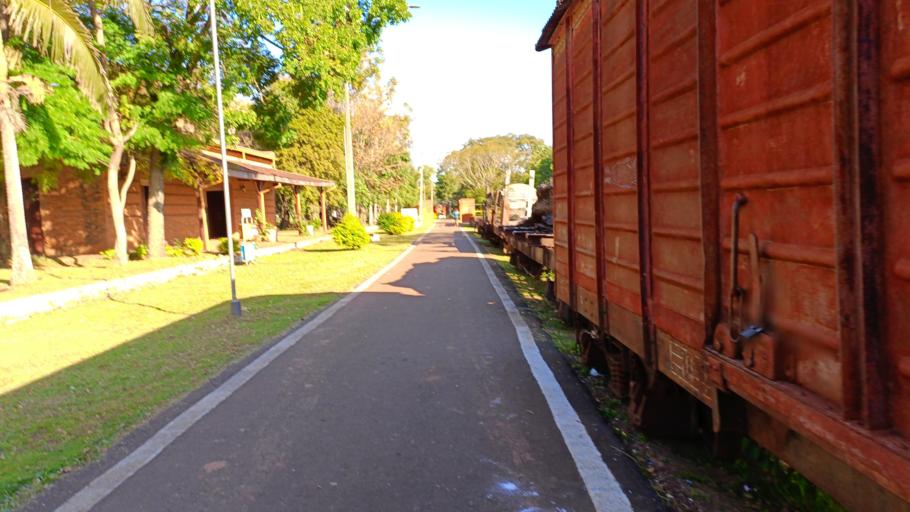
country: PY
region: Itapua
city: Carmen del Parana
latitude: -27.1602
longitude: -56.2404
